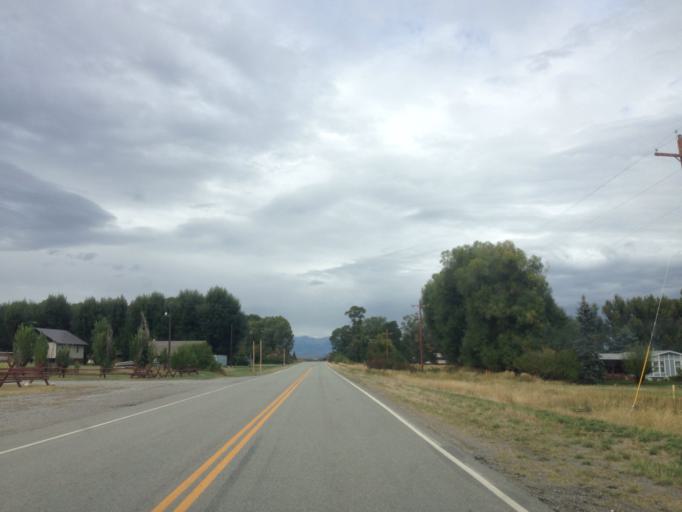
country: US
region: Montana
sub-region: Sweet Grass County
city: Big Timber
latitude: 45.7744
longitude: -109.8029
